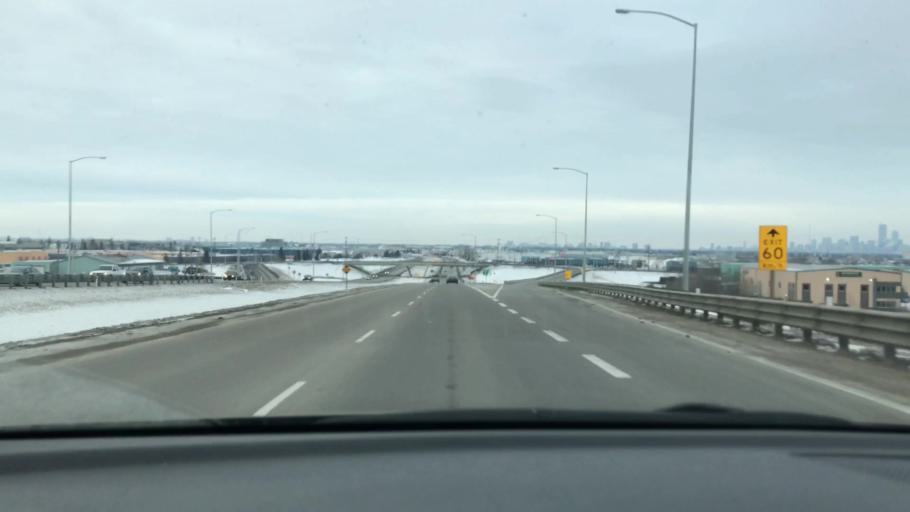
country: CA
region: Alberta
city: Sherwood Park
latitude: 53.5173
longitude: -113.3872
